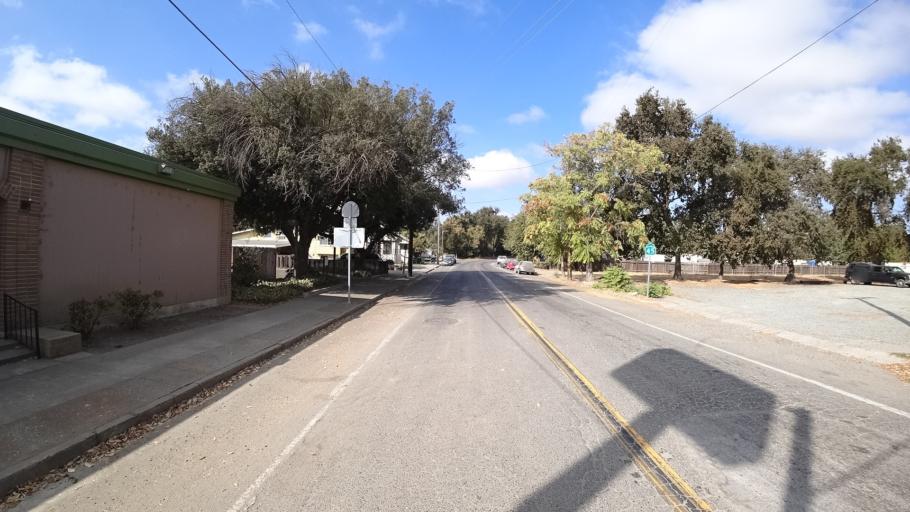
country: US
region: California
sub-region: Yolo County
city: Woodland
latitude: 38.8006
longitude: -121.7204
